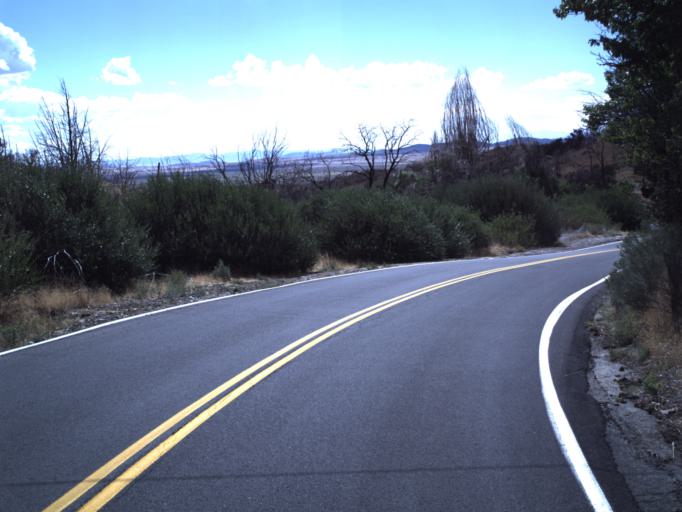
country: US
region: Utah
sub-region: Tooele County
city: Grantsville
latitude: 40.3382
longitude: -112.6106
